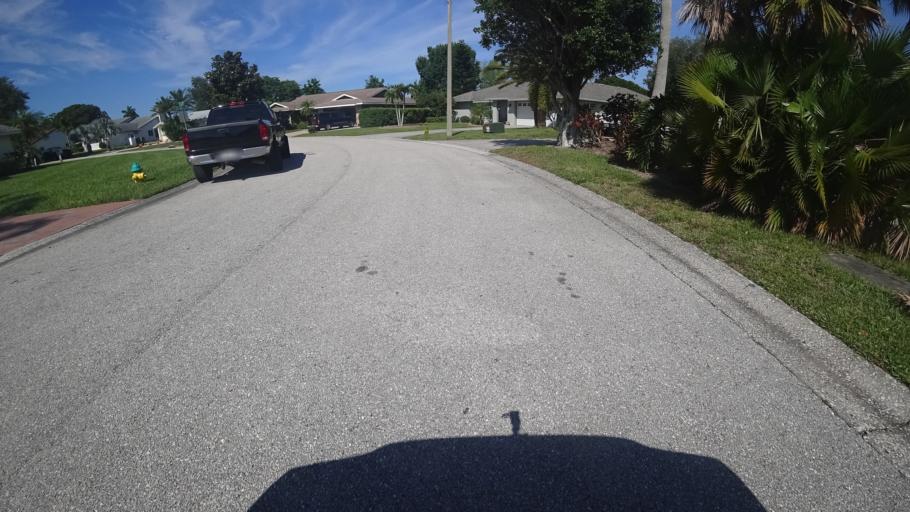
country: US
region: Florida
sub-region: Manatee County
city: West Bradenton
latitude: 27.5094
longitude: -82.6427
